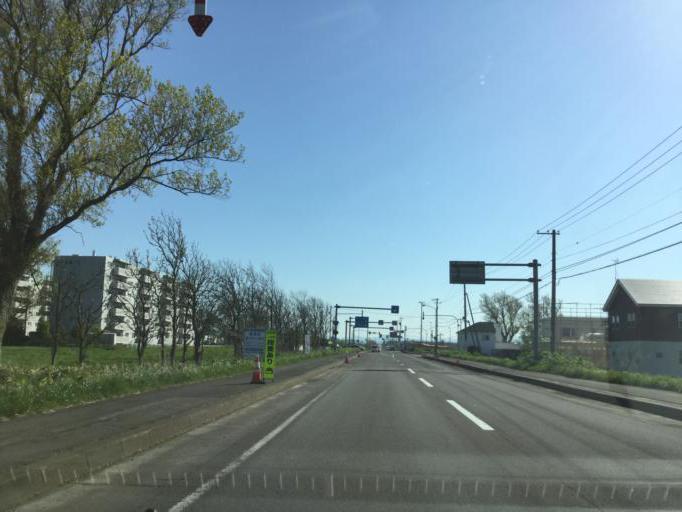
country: JP
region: Hokkaido
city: Ebetsu
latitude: 43.0589
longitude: 141.6565
